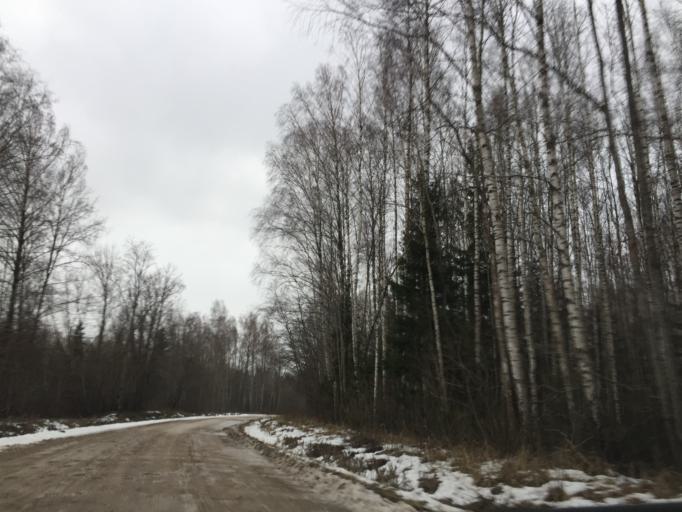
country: LV
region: Salacgrivas
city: Salacgriva
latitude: 57.6484
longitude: 24.4199
